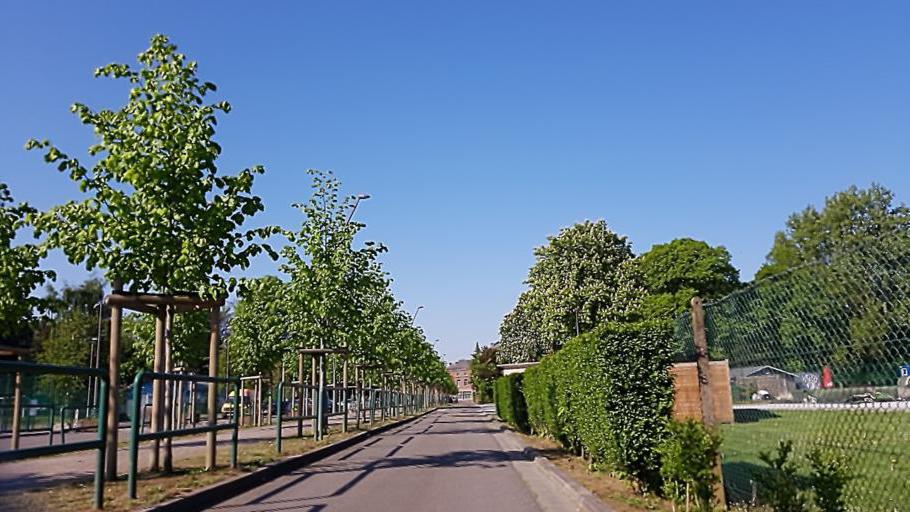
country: BE
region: Wallonia
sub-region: Province du Brabant Wallon
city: Wavre
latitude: 50.7204
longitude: 4.6189
